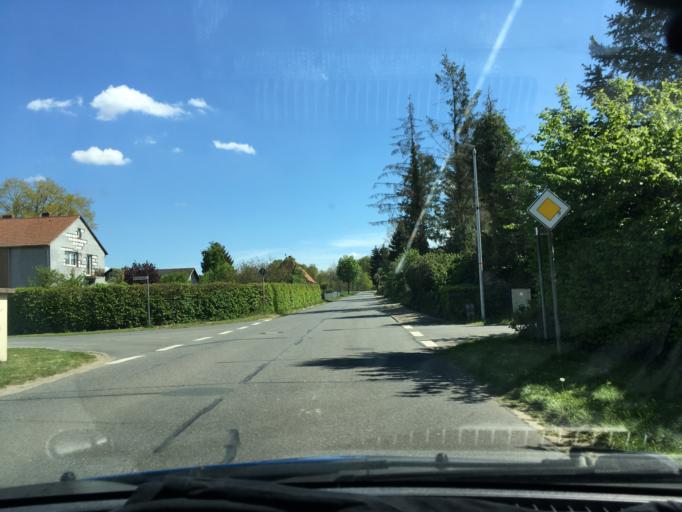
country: DE
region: Lower Saxony
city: Stoetze
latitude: 53.0677
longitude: 10.7873
